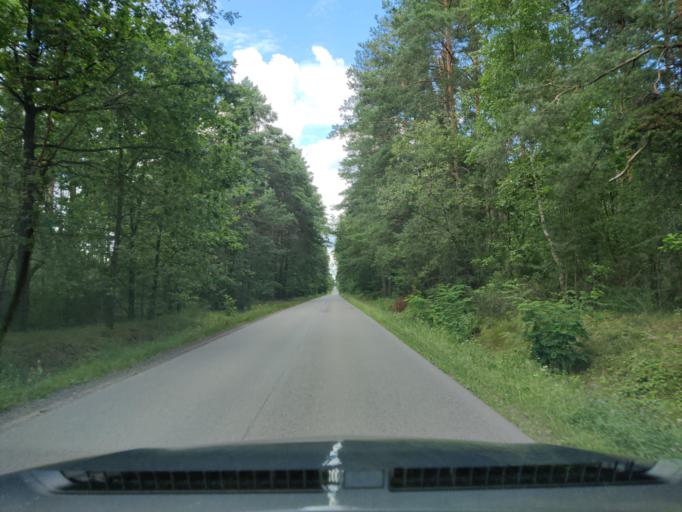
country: PL
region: Masovian Voivodeship
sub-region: Powiat wegrowski
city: Miedzna
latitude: 52.5298
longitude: 22.0790
